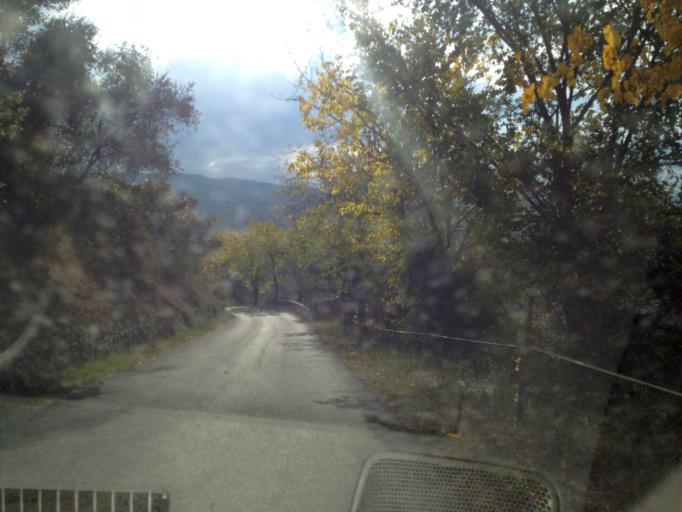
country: IT
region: Tuscany
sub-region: Province of Florence
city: Montebonello
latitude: 43.8544
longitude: 11.5000
